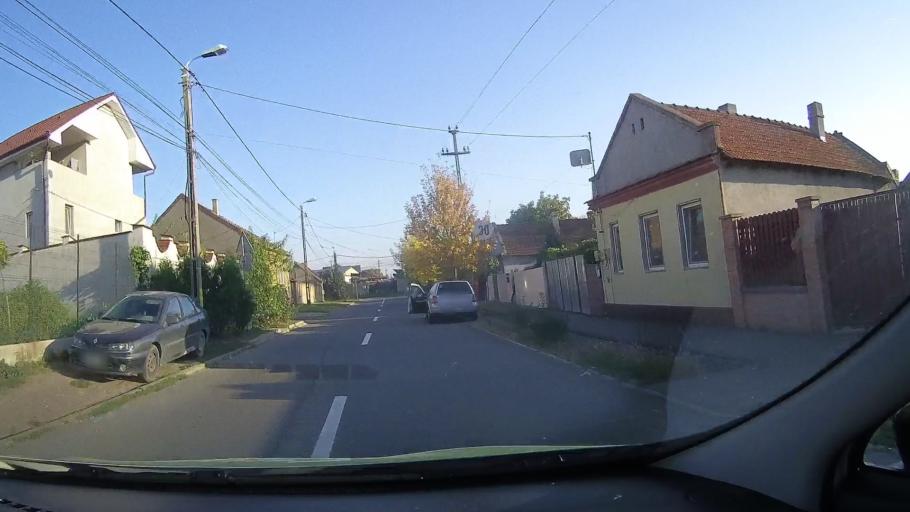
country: RO
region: Bihor
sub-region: Comuna Biharea
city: Oradea
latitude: 47.0976
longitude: 21.9003
